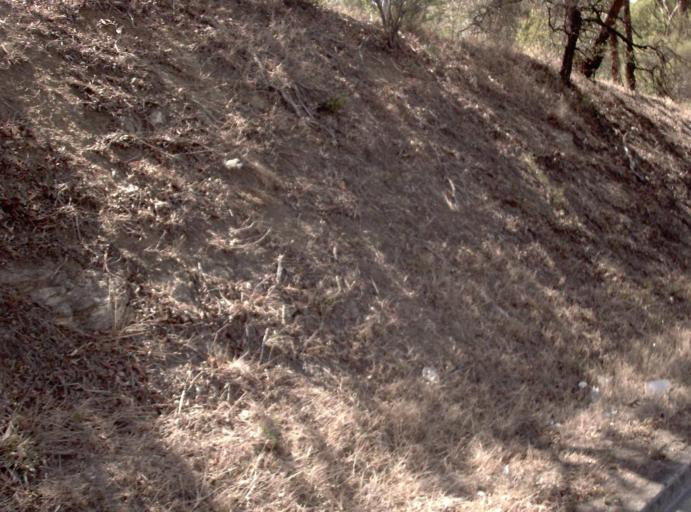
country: AU
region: Victoria
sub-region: Nillumbik
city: Eltham
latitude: -37.7357
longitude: 145.1345
